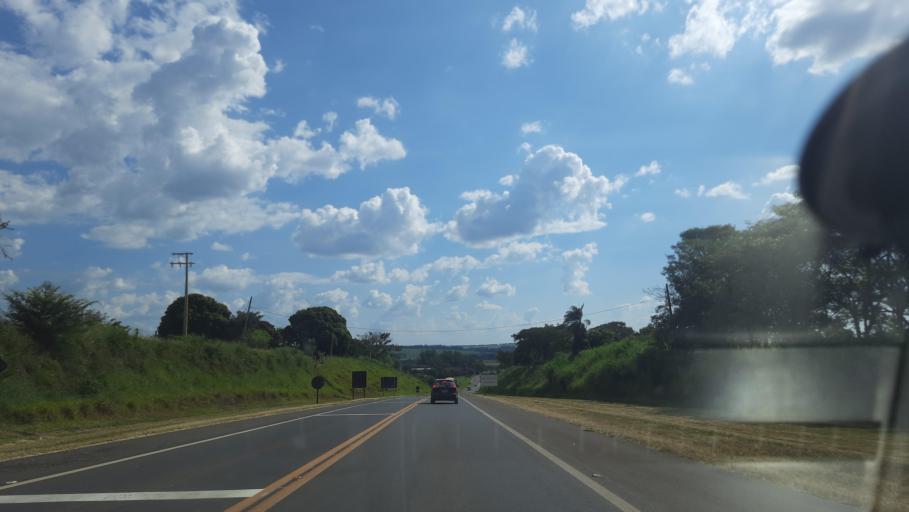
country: BR
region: Sao Paulo
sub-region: Casa Branca
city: Casa Branca
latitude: -21.7378
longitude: -46.9743
